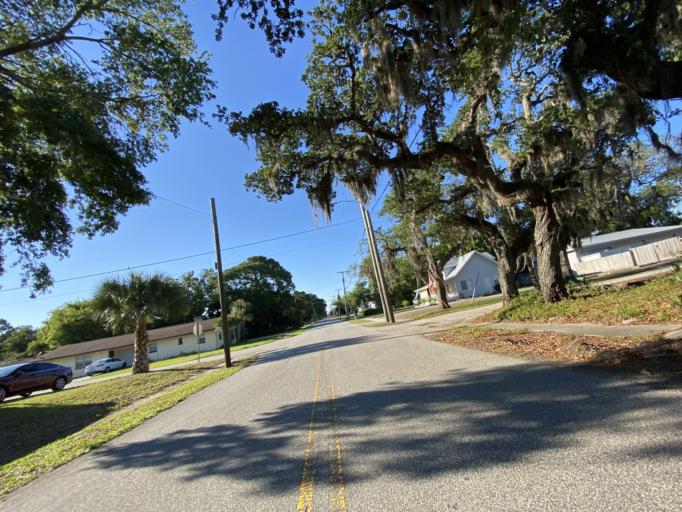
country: US
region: Florida
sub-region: Volusia County
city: Port Orange
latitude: 29.1455
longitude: -80.9924
